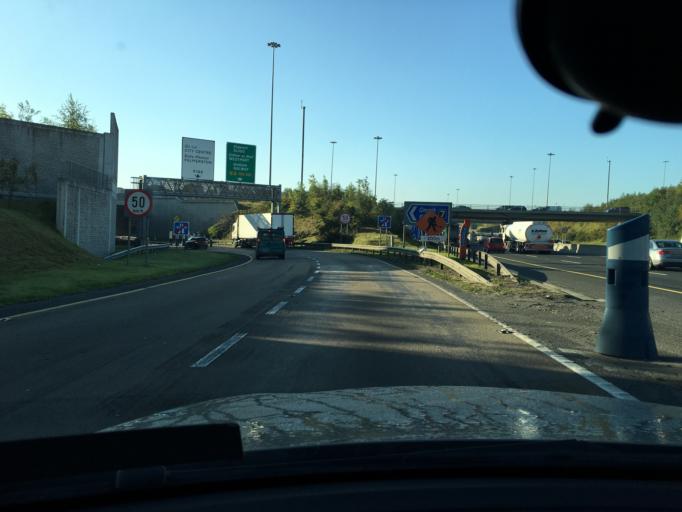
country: IE
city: Palmerstown
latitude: 53.3584
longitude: -6.3836
